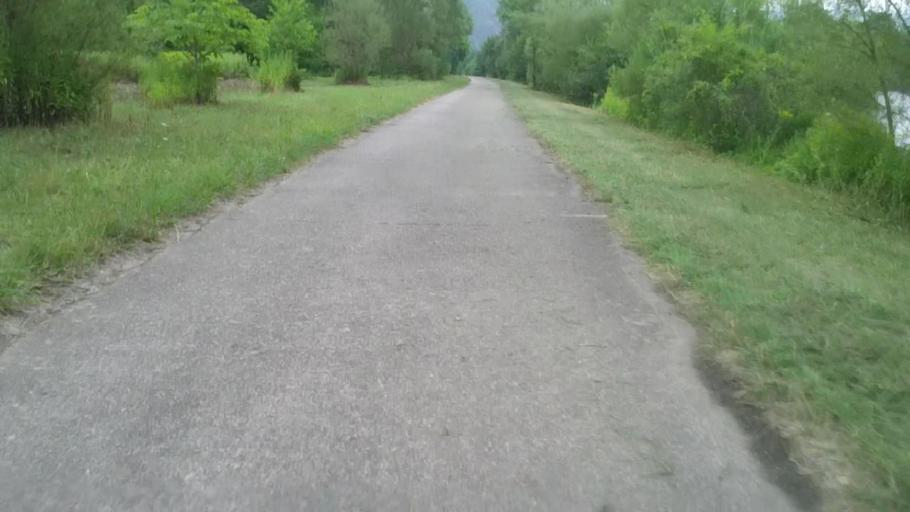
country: DE
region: Rheinland-Pfalz
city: Saarburg
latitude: 49.5953
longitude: 6.5601
